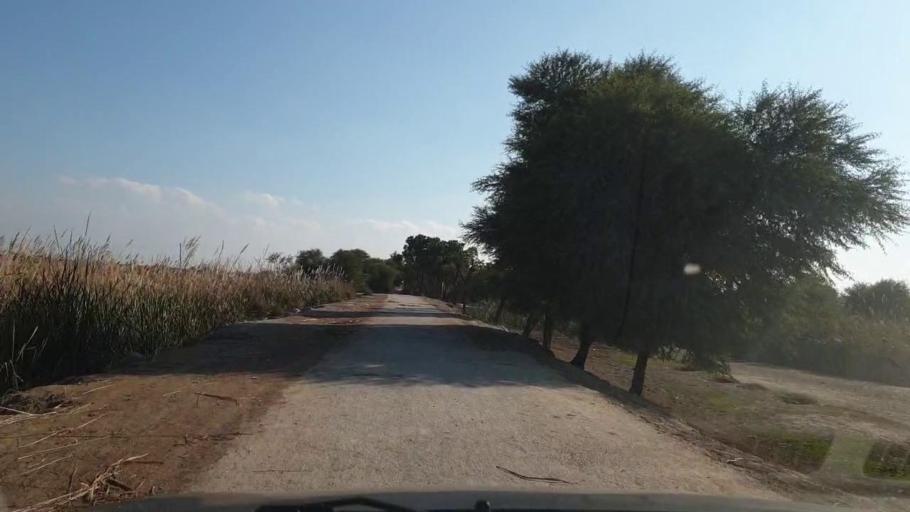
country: PK
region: Sindh
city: Sinjhoro
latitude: 25.9764
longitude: 68.7249
